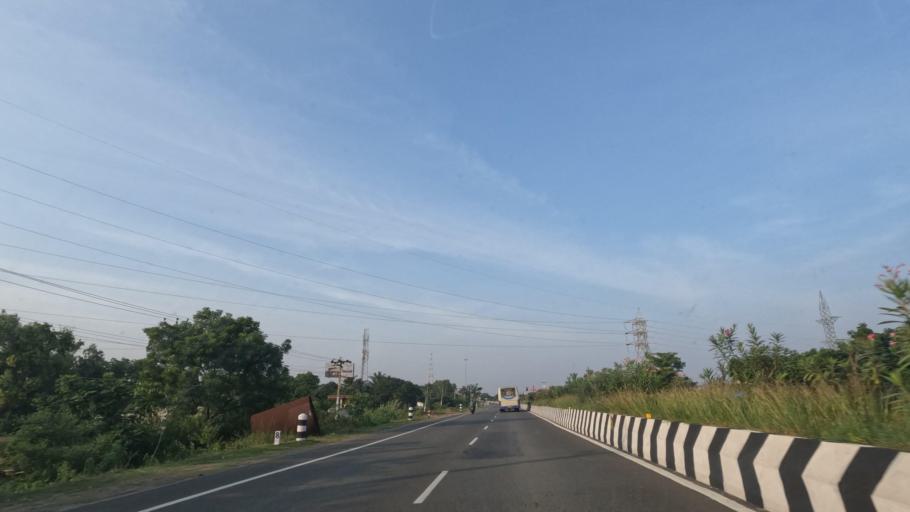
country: IN
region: Tamil Nadu
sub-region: Kancheepuram
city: Mamallapuram
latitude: 12.7022
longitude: 80.2226
